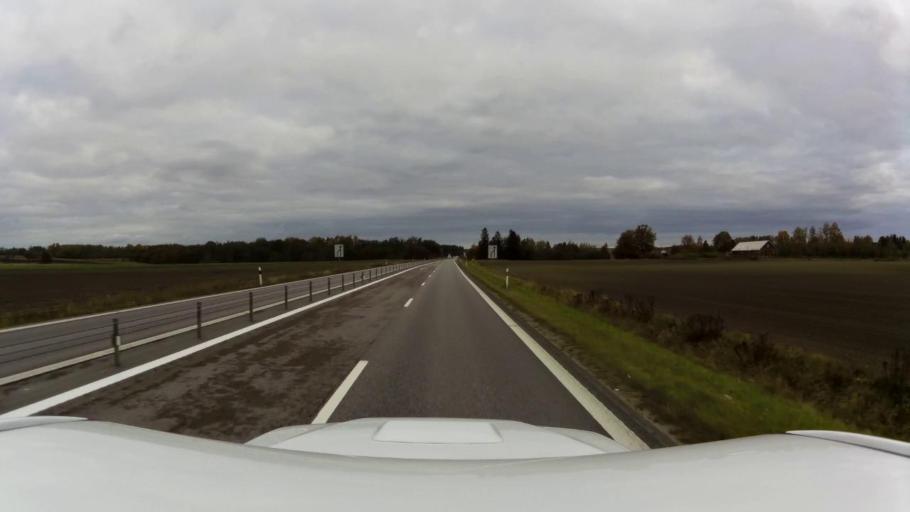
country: SE
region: OEstergoetland
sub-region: Linkopings Kommun
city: Malmslatt
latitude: 58.4504
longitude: 15.5070
